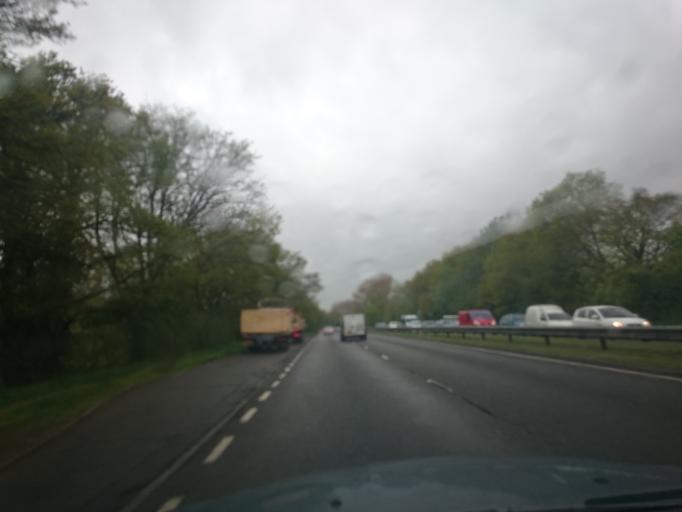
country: GB
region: England
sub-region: Surrey
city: Hale
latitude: 51.2173
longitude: -0.7838
